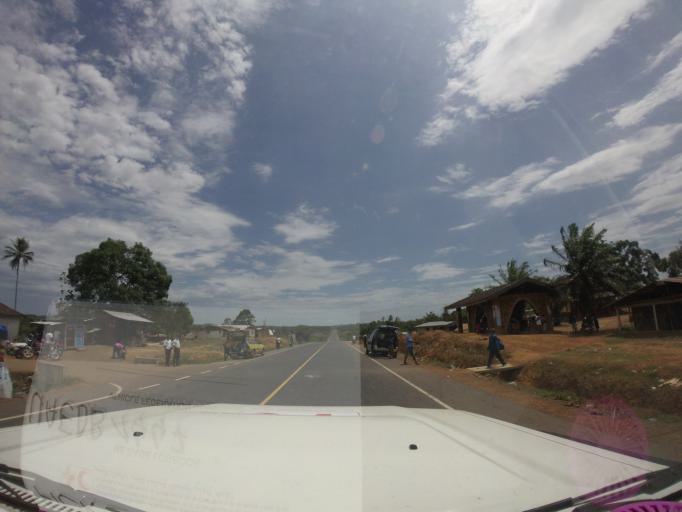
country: LR
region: Montserrado
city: Bensonville City
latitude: 6.4263
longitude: -10.4686
